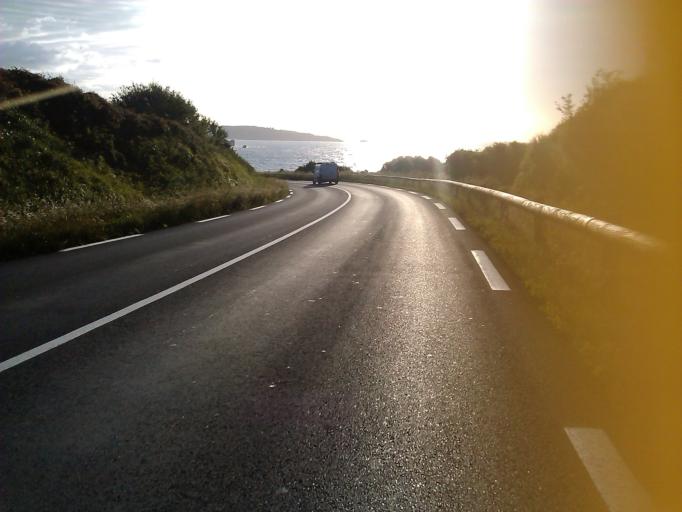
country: FR
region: Aquitaine
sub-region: Departement des Pyrenees-Atlantiques
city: Urrugne
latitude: 43.3843
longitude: -1.7233
